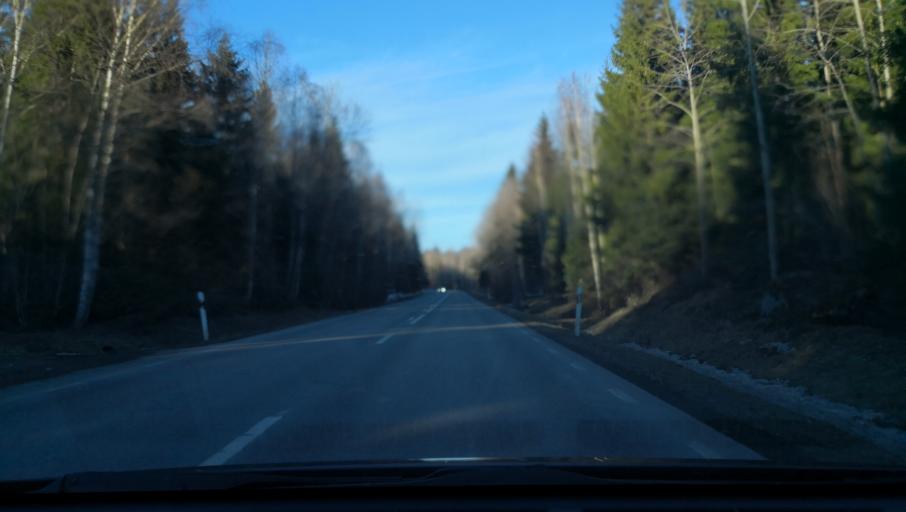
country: SE
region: Uppsala
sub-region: Osthammars Kommun
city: Gimo
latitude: 60.1992
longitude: 18.1932
